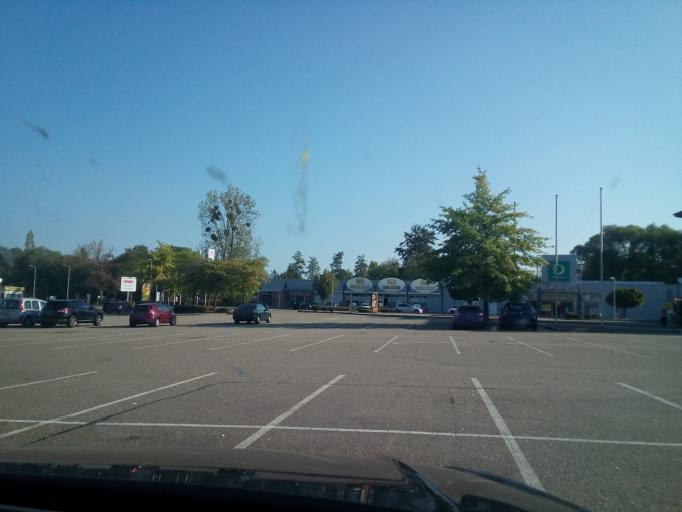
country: DE
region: Baden-Wuerttemberg
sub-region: Karlsruhe Region
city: Sinzheim
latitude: 48.7763
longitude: 8.1787
